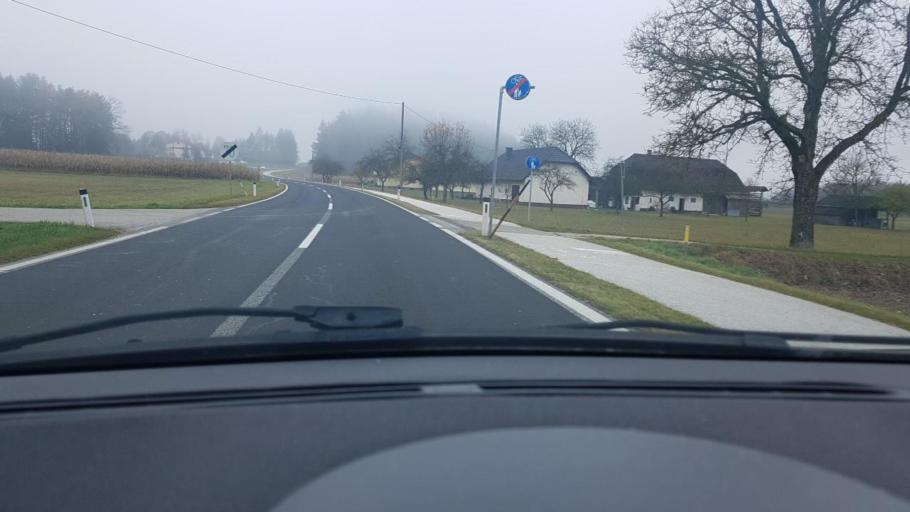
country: AT
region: Carinthia
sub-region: Politischer Bezirk Volkermarkt
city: Bleiburg/Pliberk
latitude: 46.6165
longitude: 14.8037
